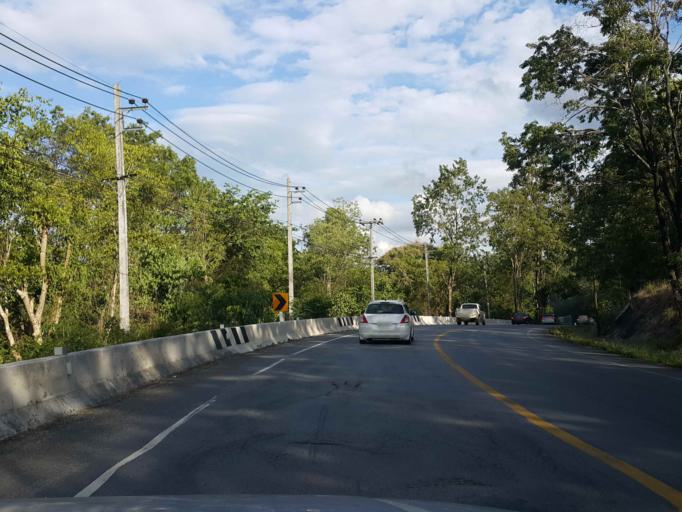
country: TH
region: Tak
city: Tak
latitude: 16.8085
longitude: 98.9940
